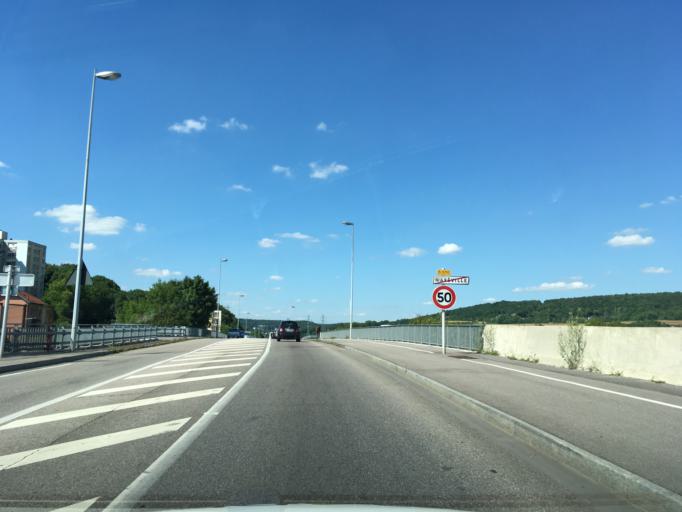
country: FR
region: Lorraine
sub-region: Departement de Meurthe-et-Moselle
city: Maxeville
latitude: 48.7184
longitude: 6.1708
